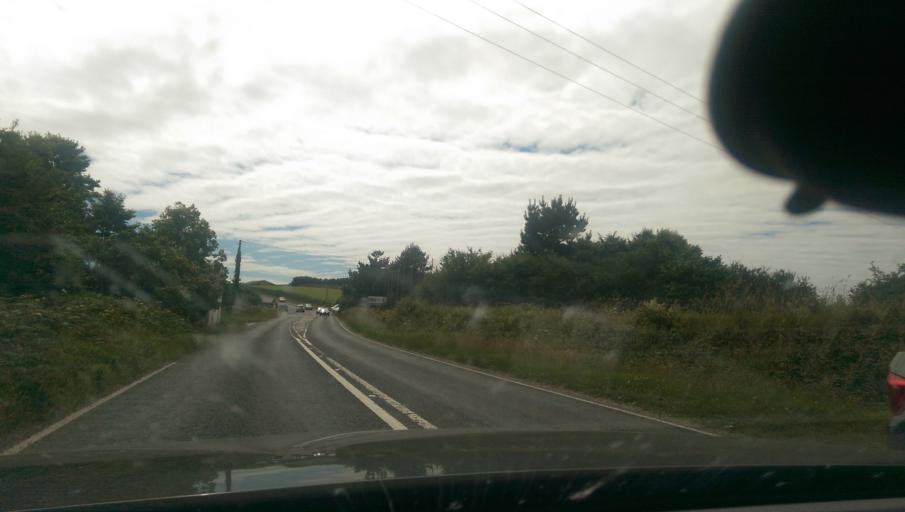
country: GB
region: England
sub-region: Cornwall
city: Wadebridge
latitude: 50.5087
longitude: -4.8803
